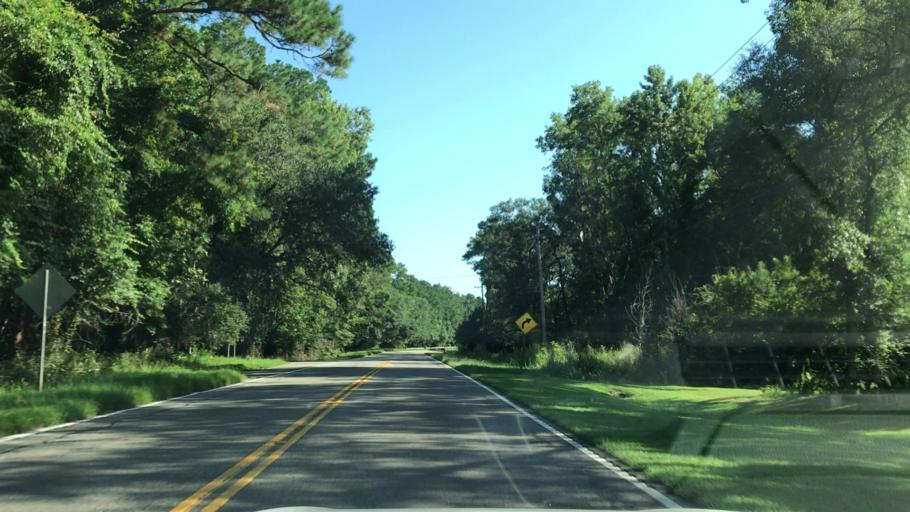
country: US
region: South Carolina
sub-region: Georgetown County
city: Georgetown
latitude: 33.4729
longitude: -79.2790
